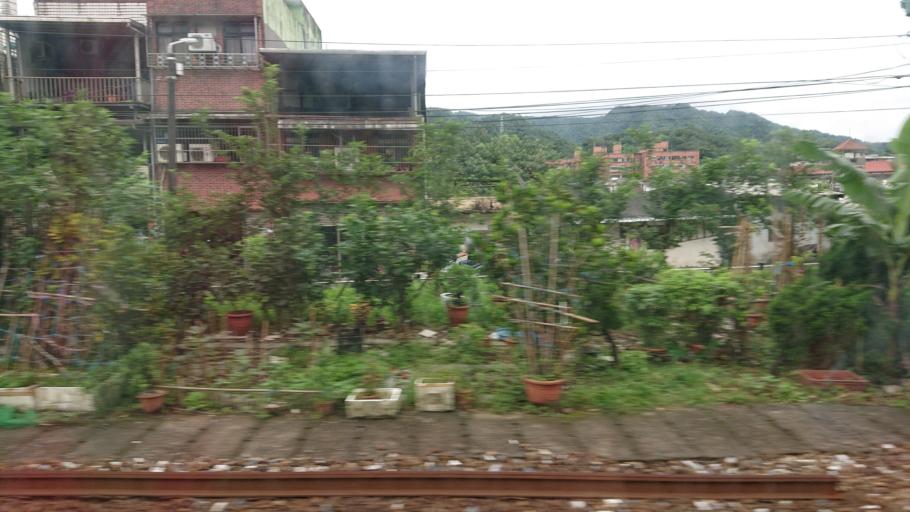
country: TW
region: Taiwan
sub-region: Keelung
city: Keelung
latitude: 25.1084
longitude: 121.8178
